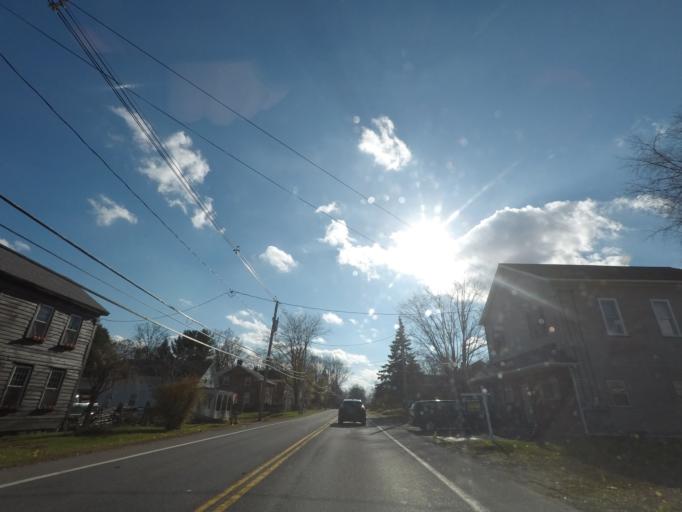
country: US
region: New York
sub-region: Schenectady County
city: East Glenville
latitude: 42.9082
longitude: -73.8956
